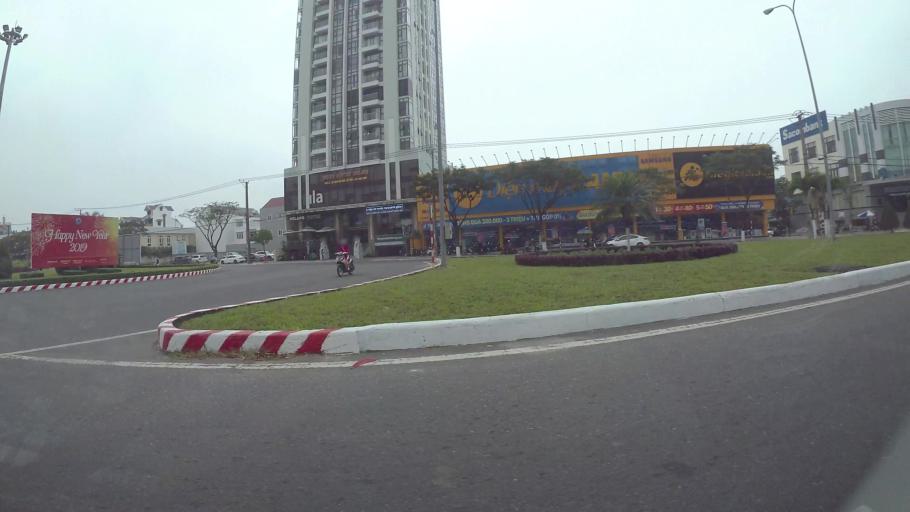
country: VN
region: Da Nang
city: Cam Le
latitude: 16.0400
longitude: 108.2108
